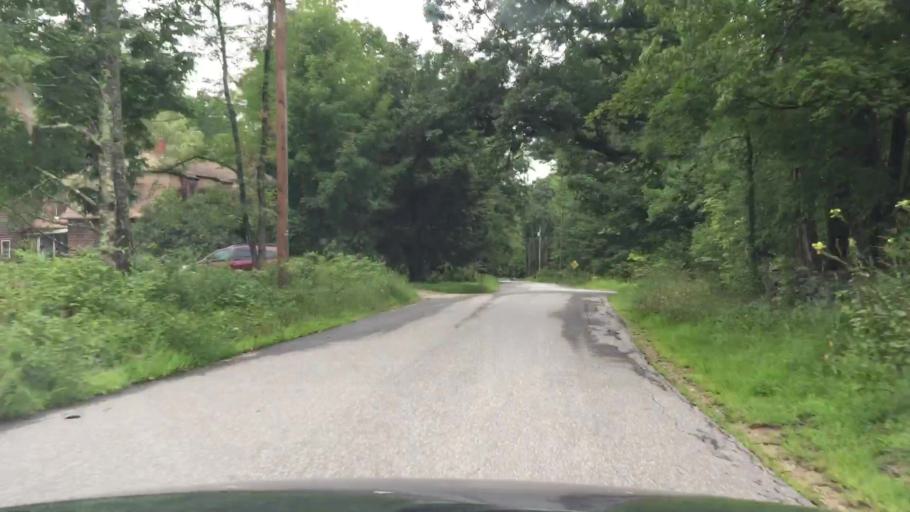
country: US
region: New Hampshire
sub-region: Carroll County
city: Center Harbor
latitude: 43.7232
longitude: -71.4928
